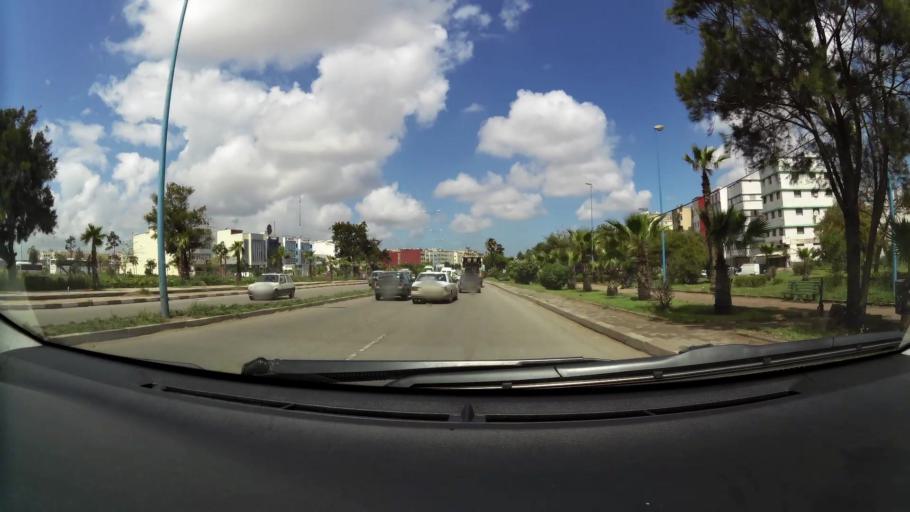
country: MA
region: Grand Casablanca
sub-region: Casablanca
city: Casablanca
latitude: 33.5346
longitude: -7.5734
